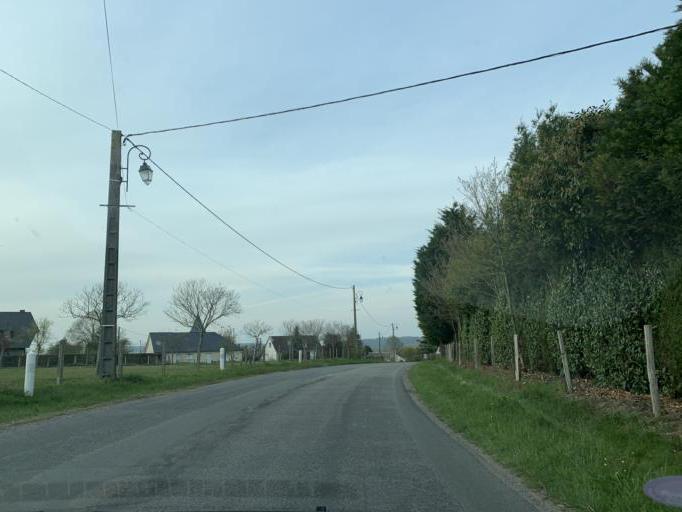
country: FR
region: Haute-Normandie
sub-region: Departement de la Seine-Maritime
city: La Mailleraye-sur-Seine
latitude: 49.4905
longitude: 0.7656
